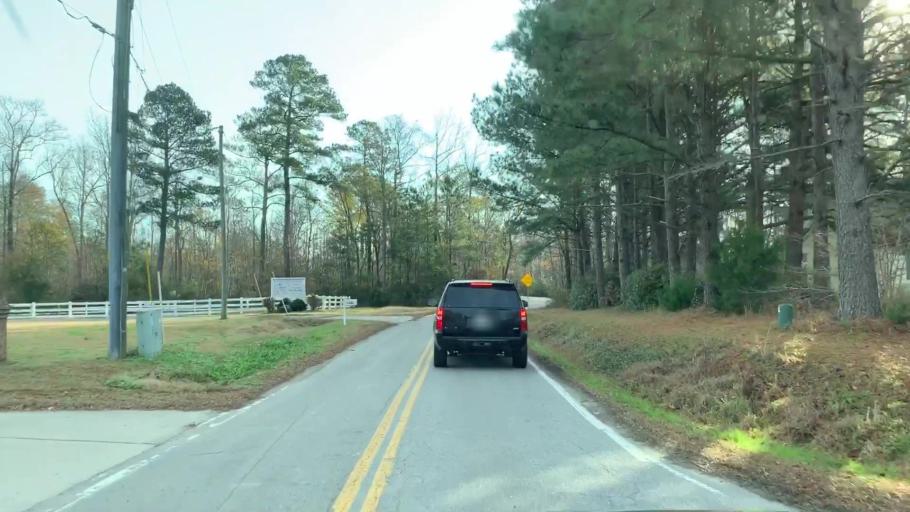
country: US
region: Virginia
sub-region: City of Virginia Beach
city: Virginia Beach
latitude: 36.6856
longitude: -75.9948
